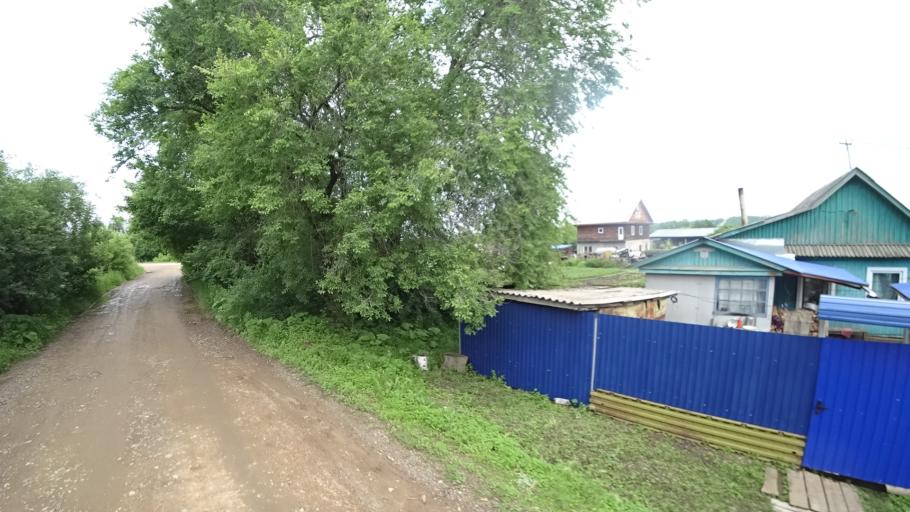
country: RU
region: Primorskiy
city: Novosysoyevka
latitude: 44.2296
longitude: 133.3666
